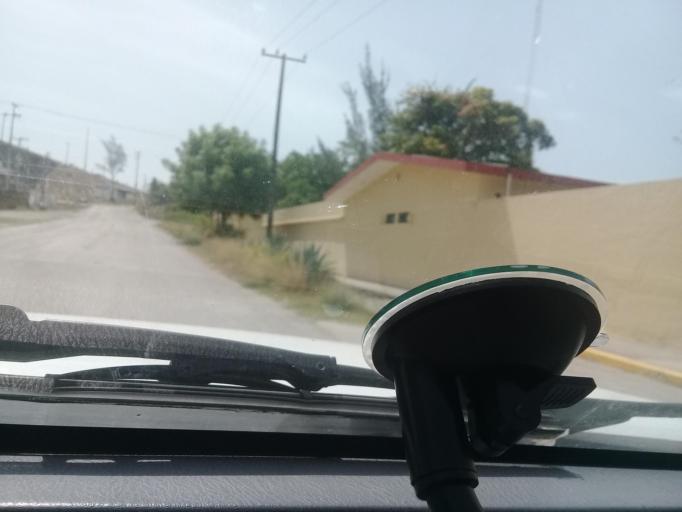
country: MX
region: Veracruz
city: Anahuac
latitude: 22.2251
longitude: -97.8346
